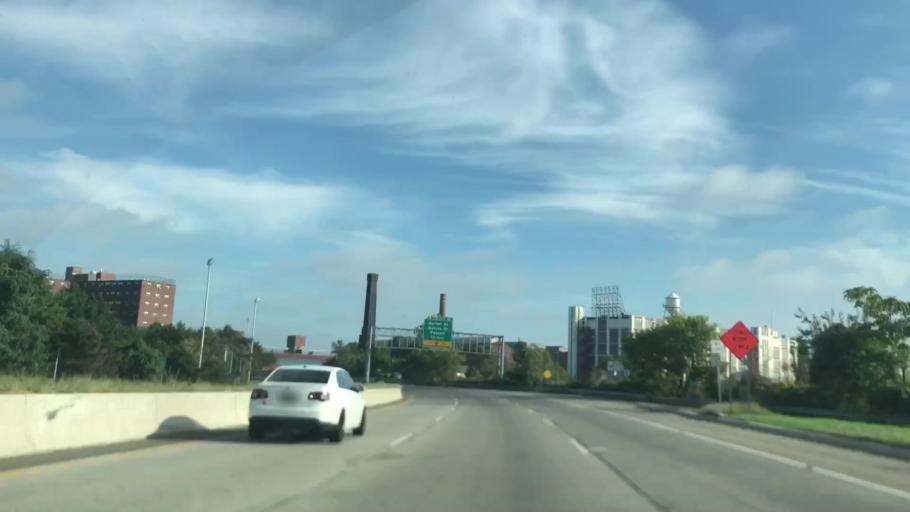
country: US
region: New Jersey
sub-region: Passaic County
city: Passaic
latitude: 40.8577
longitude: -74.1207
